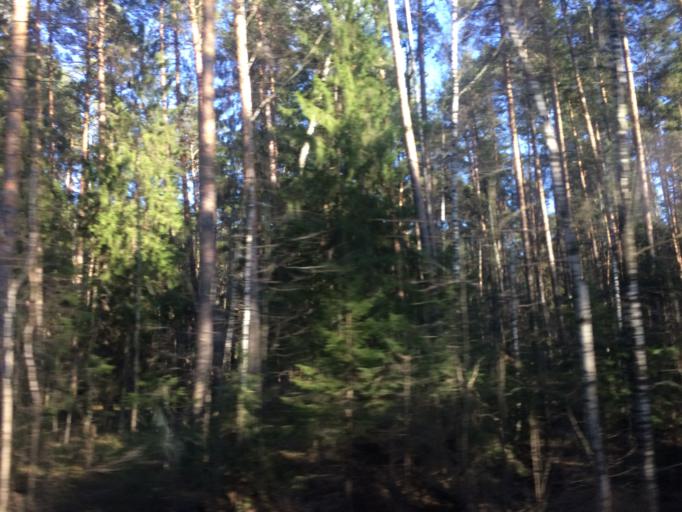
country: RU
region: Tatarstan
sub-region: Zelenodol'skiy Rayon
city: Vasil'yevo
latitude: 55.8913
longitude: 48.7264
